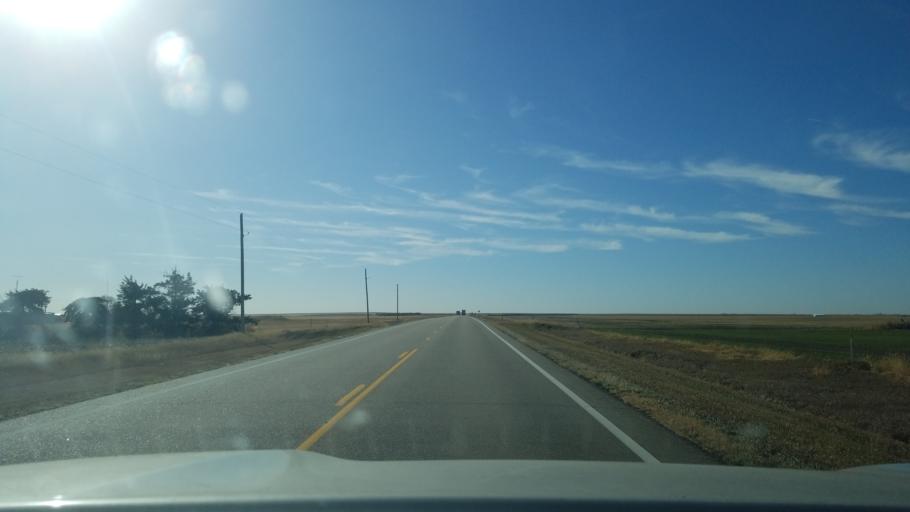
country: US
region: Kansas
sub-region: Ness County
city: Ness City
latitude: 38.3860
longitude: -99.8983
